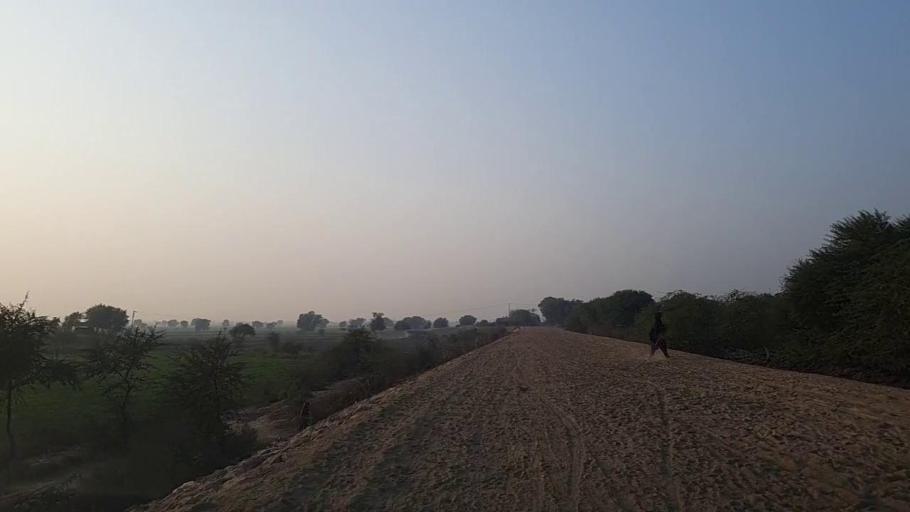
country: PK
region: Sindh
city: Sann
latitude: 26.1766
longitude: 68.0982
